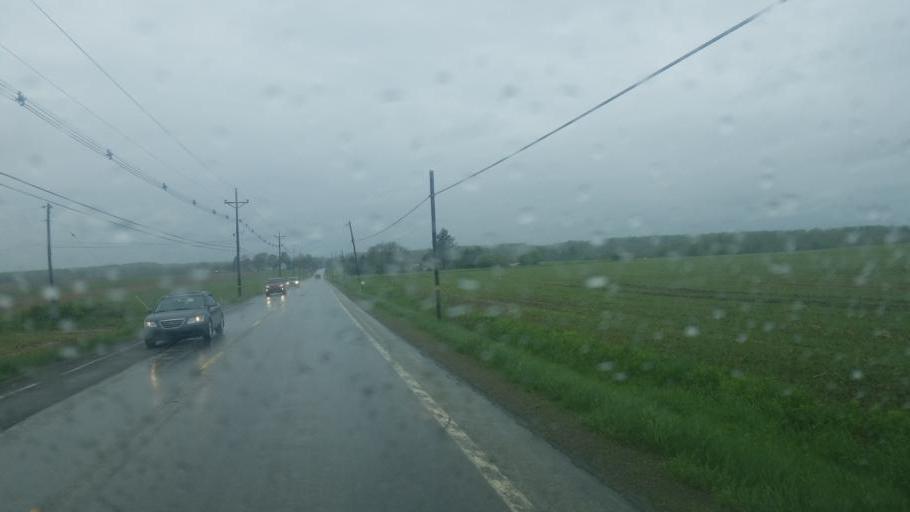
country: US
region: Pennsylvania
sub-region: Forest County
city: Tionesta
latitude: 41.3952
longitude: -79.3368
